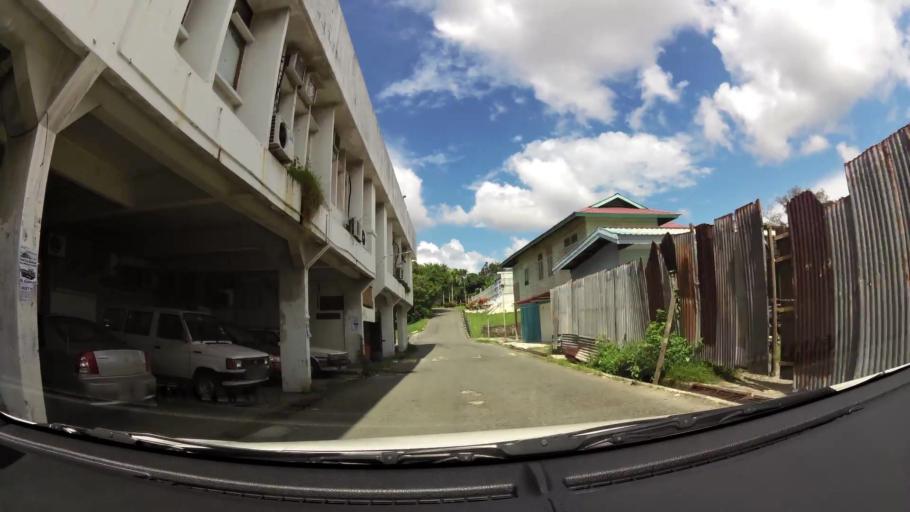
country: BN
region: Brunei and Muara
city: Bandar Seri Begawan
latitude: 4.9676
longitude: 114.9468
